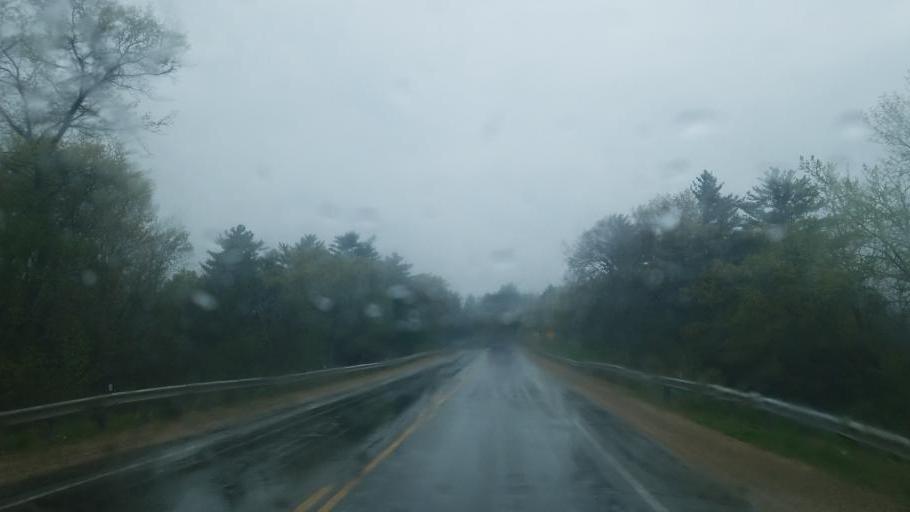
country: US
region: Wisconsin
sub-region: Sauk County
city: Reedsburg
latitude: 43.5798
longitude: -90.1155
